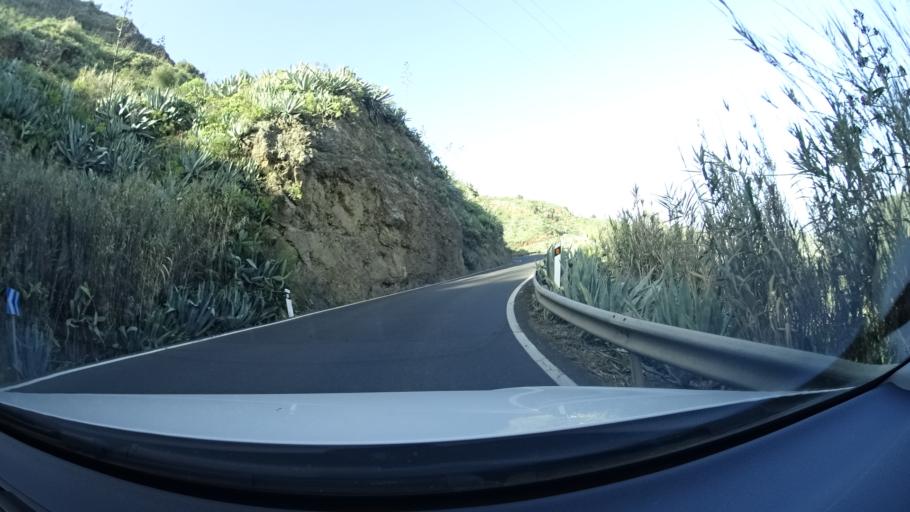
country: ES
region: Canary Islands
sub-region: Provincia de Las Palmas
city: Vega de San Mateo
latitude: 28.0214
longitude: -15.5504
